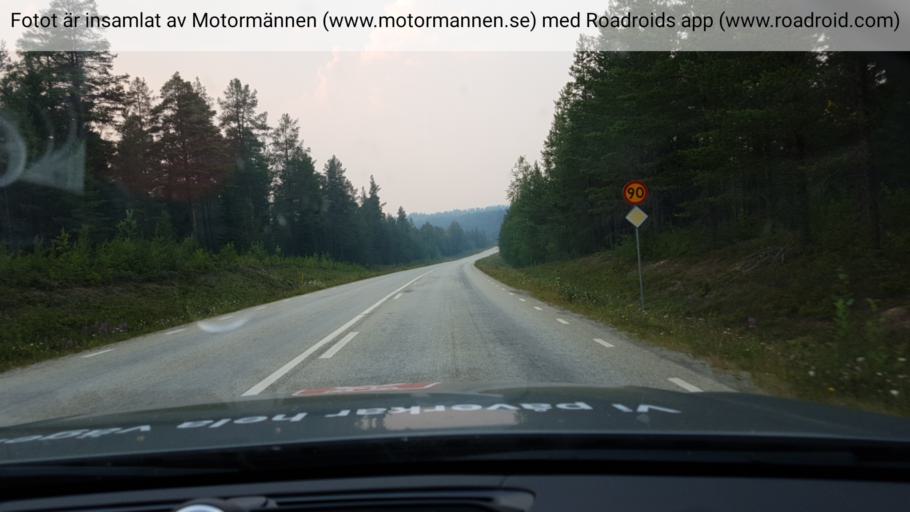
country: SE
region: Jaemtland
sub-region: Bergs Kommun
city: Hoverberg
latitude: 62.5063
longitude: 14.1976
